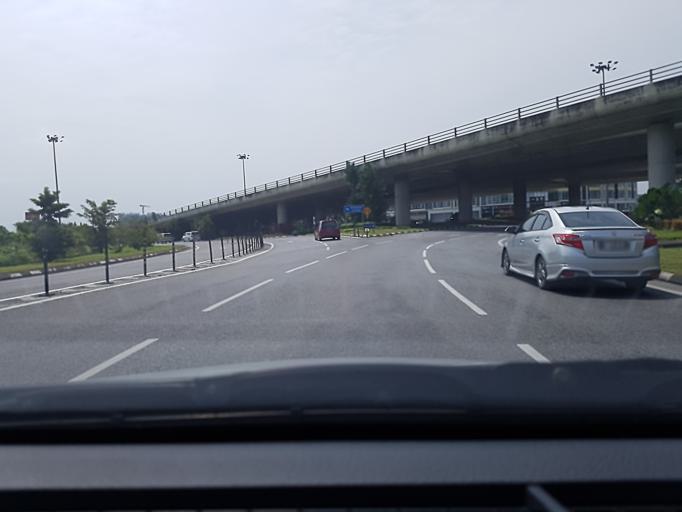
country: MY
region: Sarawak
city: Kuching
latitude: 1.5047
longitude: 110.3478
